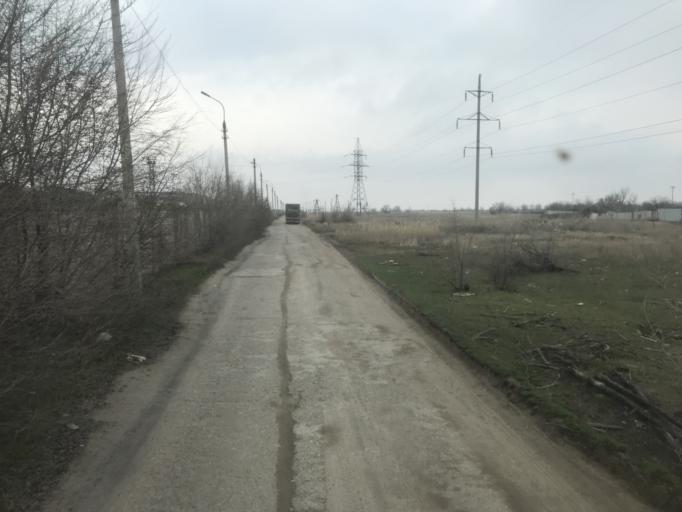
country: RU
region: Volgograd
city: Krasnoslobodsk
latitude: 48.5316
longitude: 44.5872
